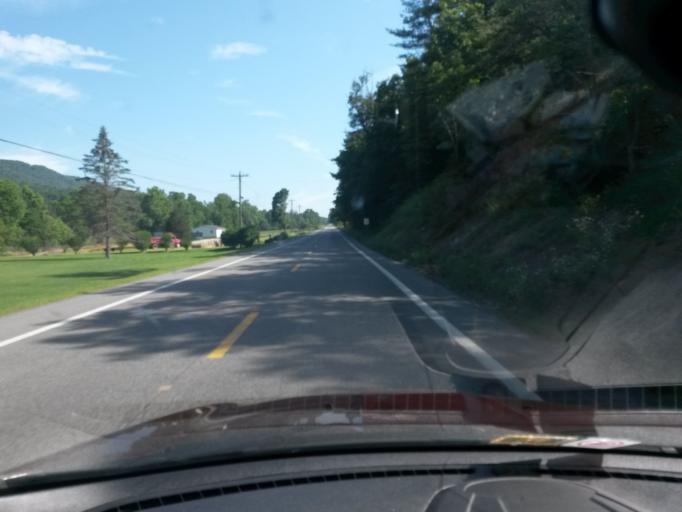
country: US
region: Virginia
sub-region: Shenandoah County
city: Basye
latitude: 38.7836
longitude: -78.8955
